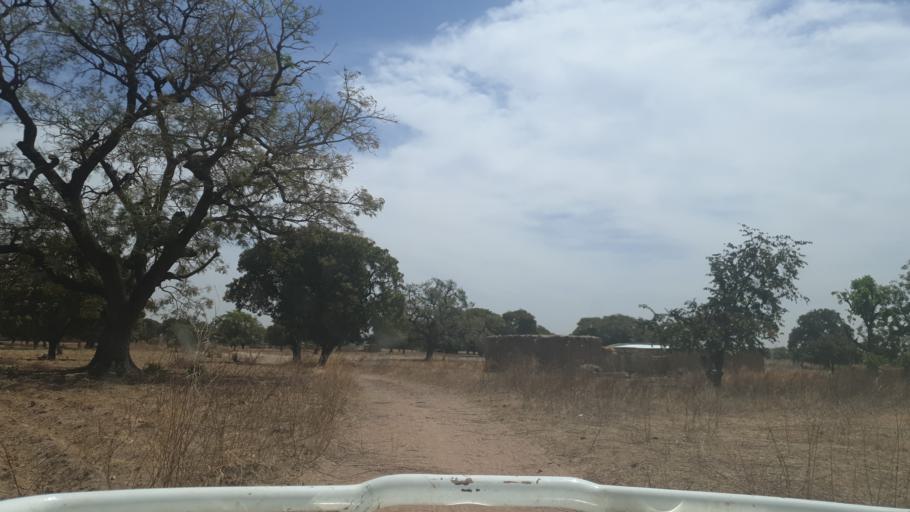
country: ML
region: Sikasso
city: Yorosso
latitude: 12.2919
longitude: -4.6605
